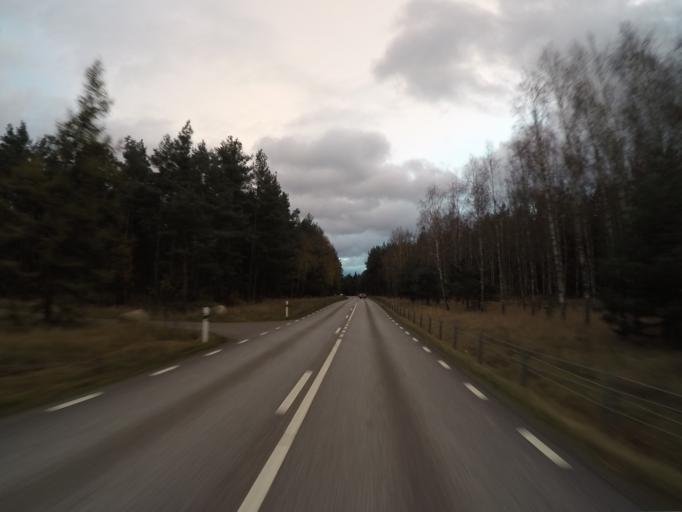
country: SE
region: Skane
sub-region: Kristianstads Kommun
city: Degeberga
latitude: 55.9178
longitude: 14.0730
